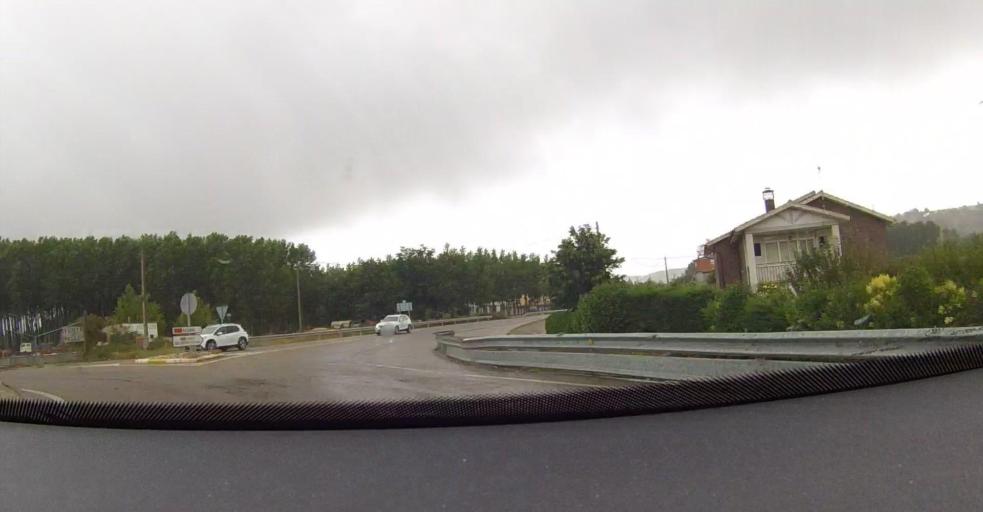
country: ES
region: Castille and Leon
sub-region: Provincia de Palencia
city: Saldana
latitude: 42.5131
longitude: -4.7394
